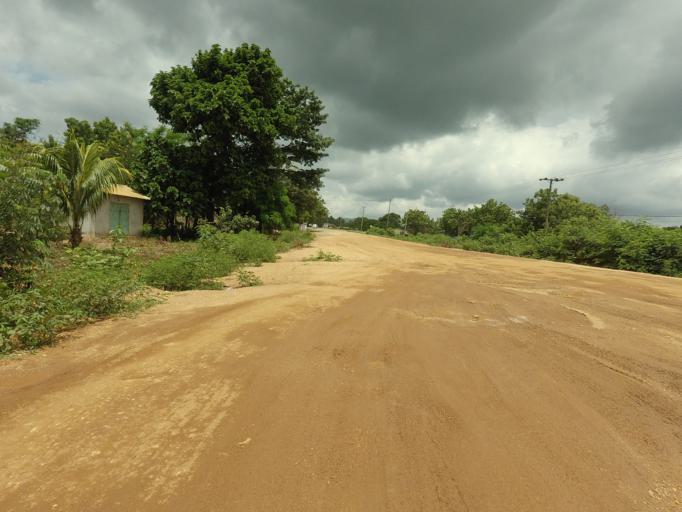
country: GH
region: Volta
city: Ho
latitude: 6.6440
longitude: 0.2983
